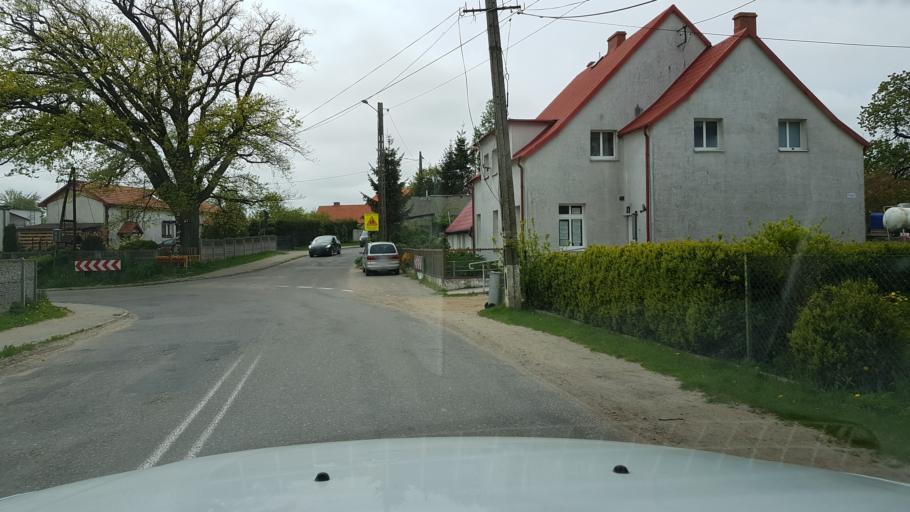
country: PL
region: Pomeranian Voivodeship
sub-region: Powiat slupski
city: Ustka
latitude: 54.5211
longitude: 16.7659
